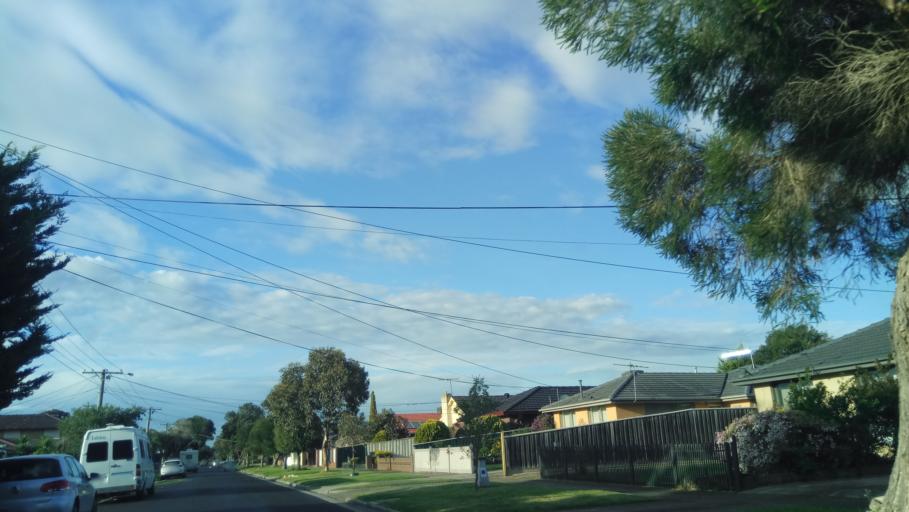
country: AU
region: Victoria
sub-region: Hobsons Bay
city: Laverton
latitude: -37.8673
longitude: 144.7826
